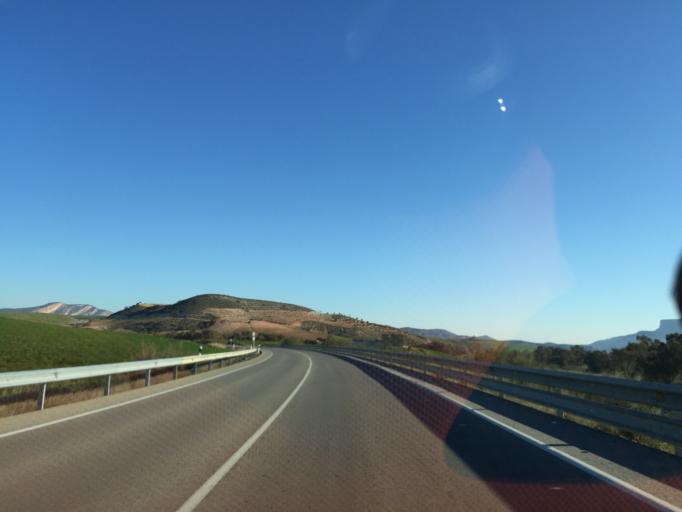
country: ES
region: Andalusia
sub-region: Provincia de Malaga
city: Ardales
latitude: 36.9012
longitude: -4.8409
